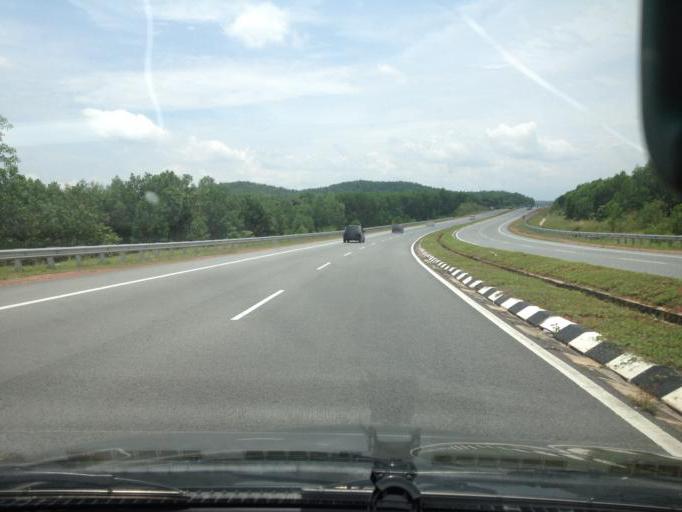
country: MY
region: Kedah
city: Sungai Petani
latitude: 5.6180
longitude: 100.5545
